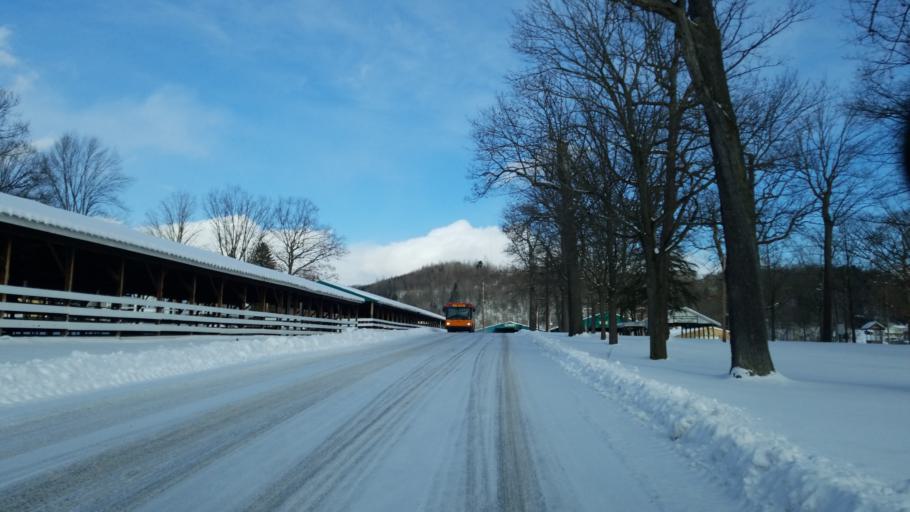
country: US
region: Pennsylvania
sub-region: Clearfield County
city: Clearfield
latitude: 41.0309
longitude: -78.4467
